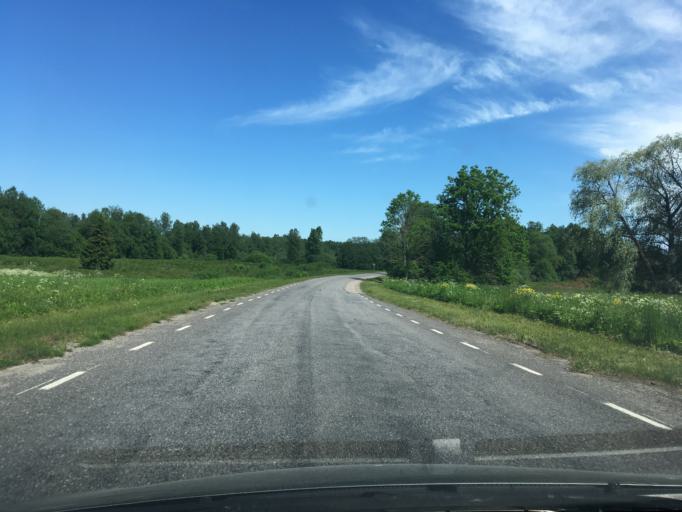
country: EE
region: Raplamaa
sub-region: Rapla vald
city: Rapla
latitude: 59.0480
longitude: 24.8802
